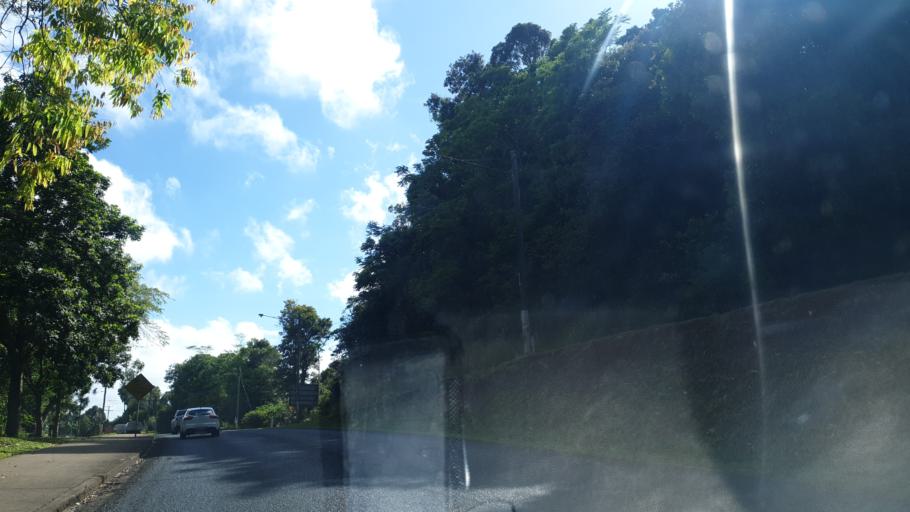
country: AU
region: Queensland
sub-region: Tablelands
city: Atherton
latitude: -17.3545
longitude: 145.5876
